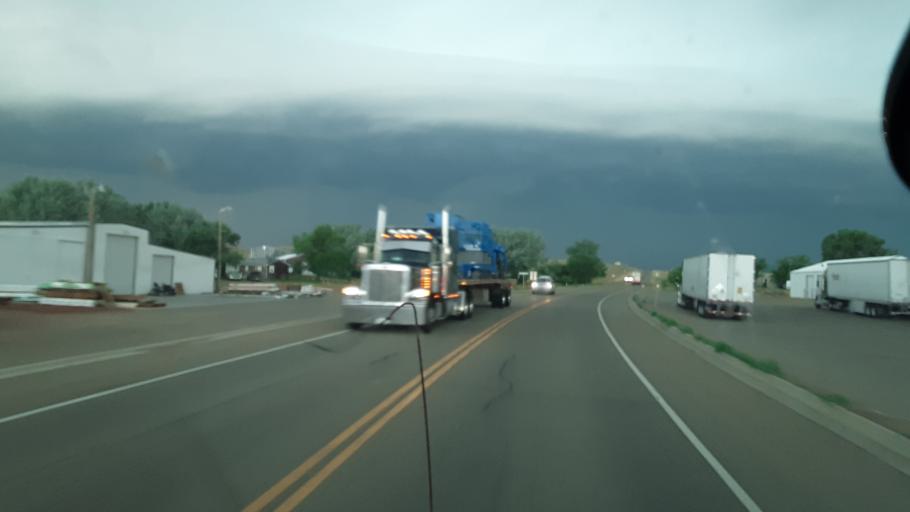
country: US
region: Montana
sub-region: Powder River County
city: Broadus
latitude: 45.4443
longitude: -105.4234
